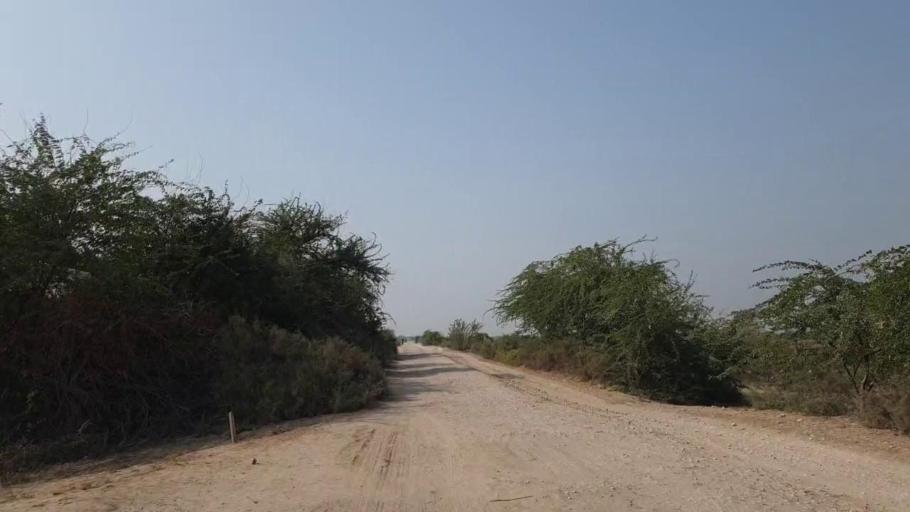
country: PK
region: Sindh
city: Kario
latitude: 24.9365
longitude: 68.5509
